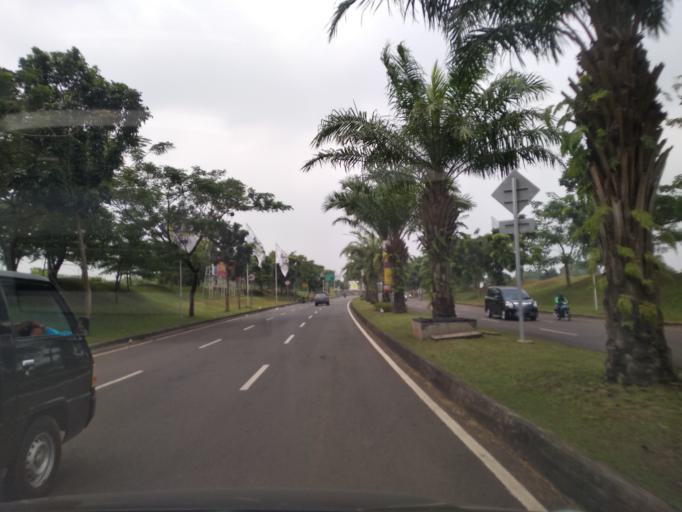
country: ID
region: West Java
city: Bekasi
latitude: -6.2925
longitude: 107.0458
